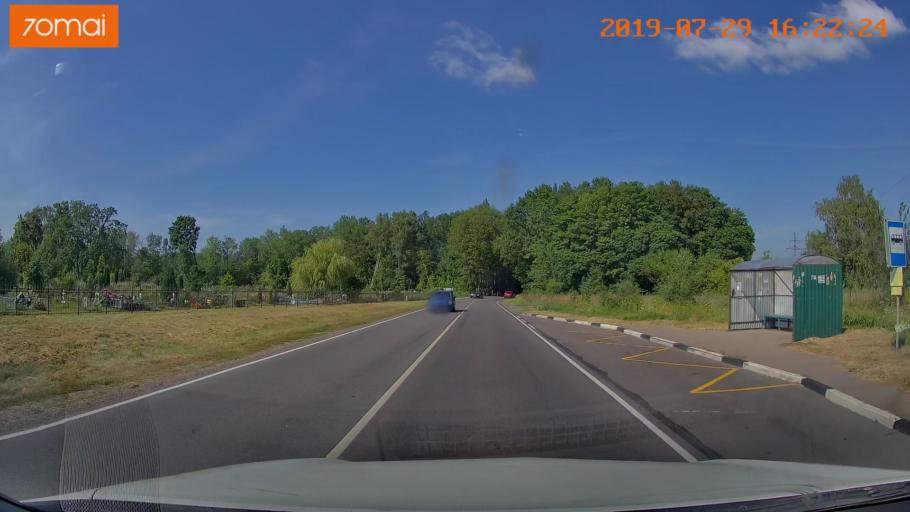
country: RU
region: Kaliningrad
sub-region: Gorod Kaliningrad
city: Baltiysk
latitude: 54.6977
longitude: 19.9386
